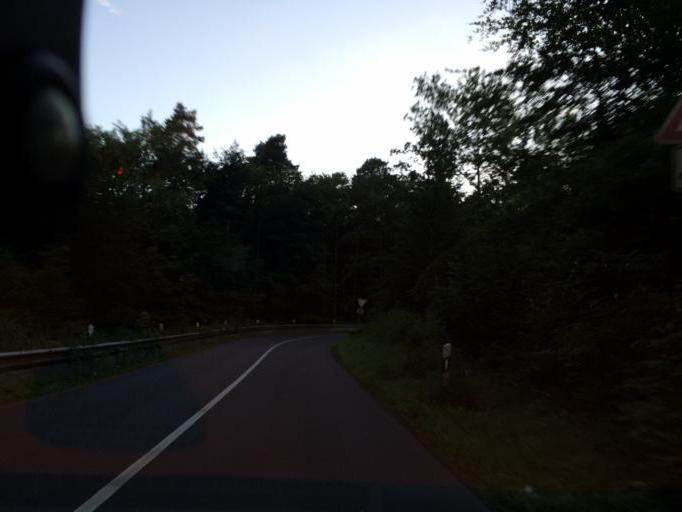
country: DE
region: North Rhine-Westphalia
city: Sankt Augustin
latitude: 50.7328
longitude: 7.1726
